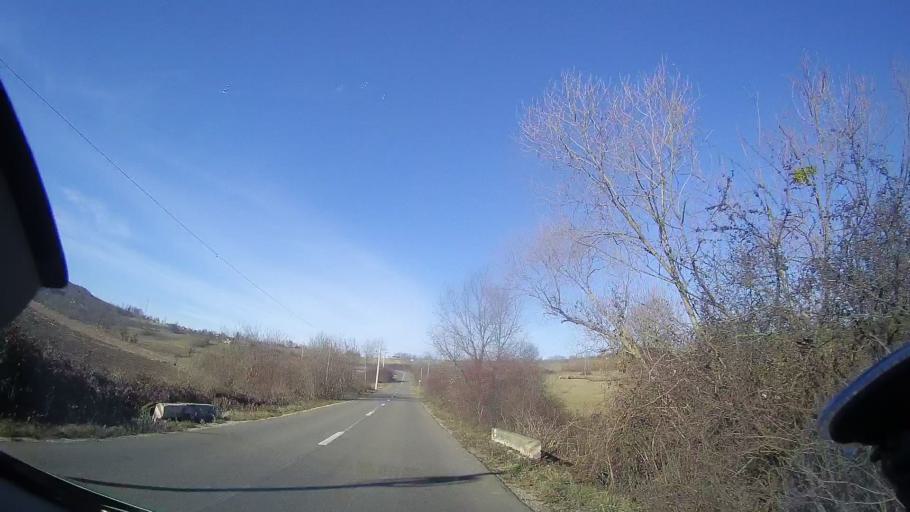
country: RO
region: Bihor
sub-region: Comuna Suncuius
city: Balnaca
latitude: 46.9692
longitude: 22.5486
